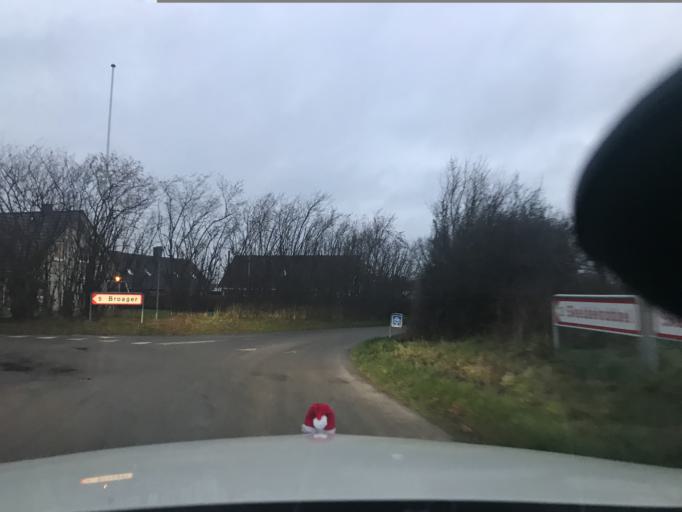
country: DK
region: South Denmark
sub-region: Sonderborg Kommune
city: Dybbol
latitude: 54.8587
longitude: 9.7270
